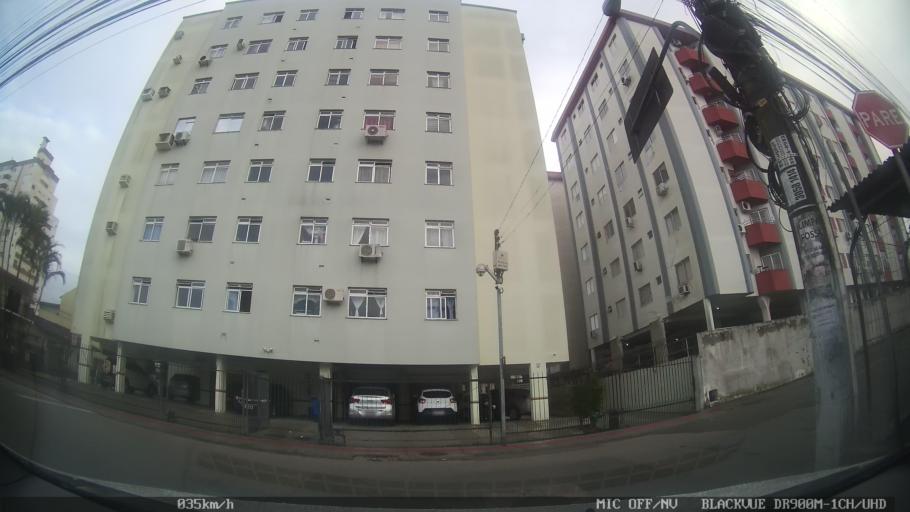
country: BR
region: Santa Catarina
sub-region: Sao Jose
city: Campinas
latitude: -27.5766
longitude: -48.6100
